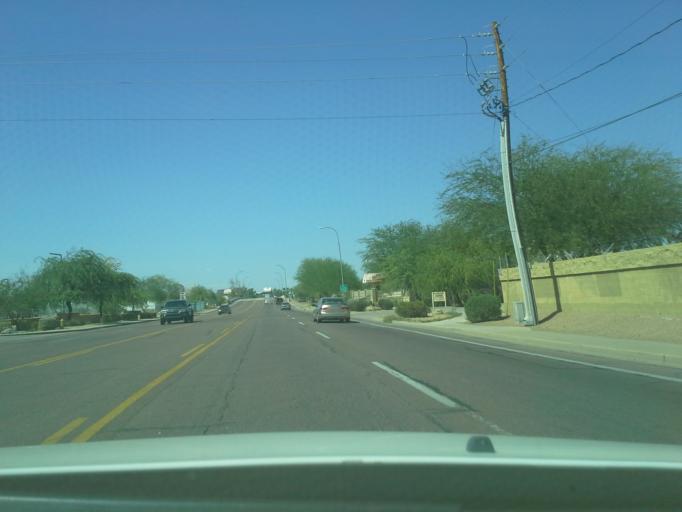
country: US
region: Arizona
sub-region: Maricopa County
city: Phoenix
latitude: 33.4175
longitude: -112.0647
